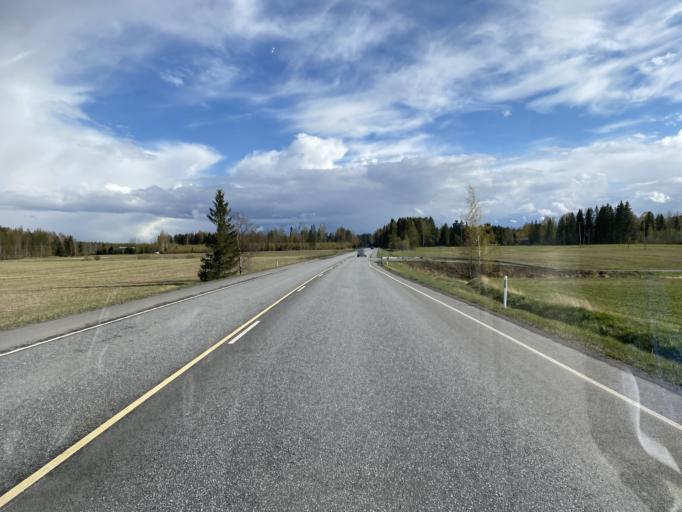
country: FI
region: Pirkanmaa
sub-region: Tampere
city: Lempaeaelae
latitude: 61.2889
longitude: 23.7429
